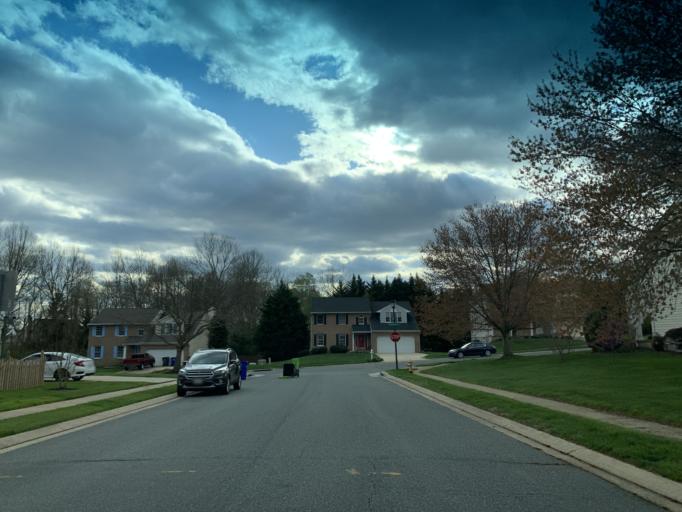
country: US
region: Maryland
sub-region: Harford County
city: South Bel Air
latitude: 39.5441
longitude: -76.3177
